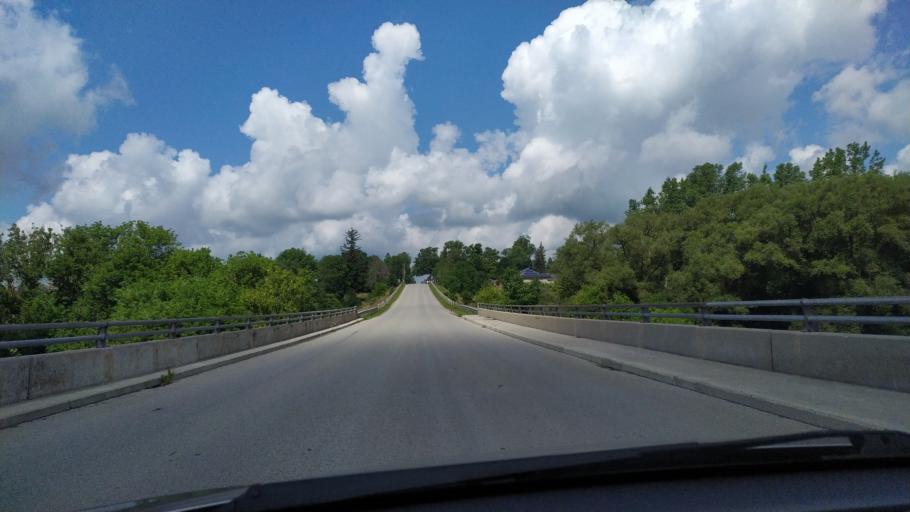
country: CA
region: Ontario
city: Huron East
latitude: 43.4594
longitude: -81.2024
